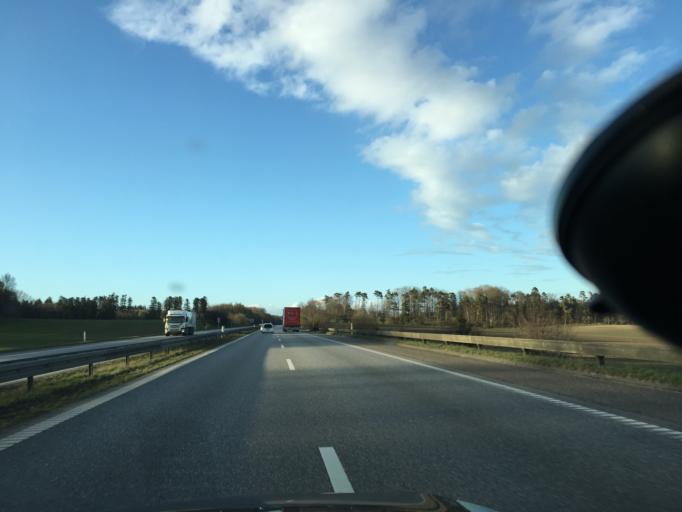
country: DK
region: North Denmark
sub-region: Rebild Kommune
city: Stovring
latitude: 56.9135
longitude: 9.8409
